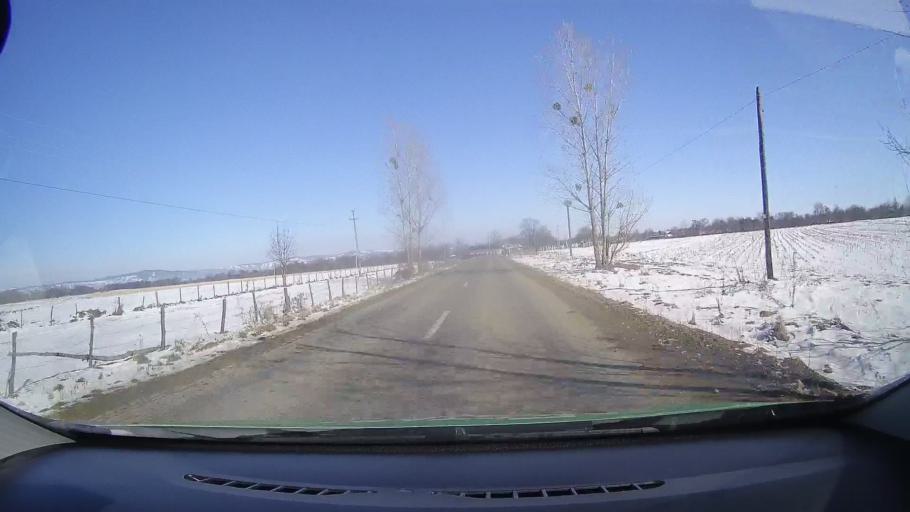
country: RO
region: Brasov
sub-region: Oras Victoria
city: Victoria
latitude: 45.7396
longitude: 24.7351
